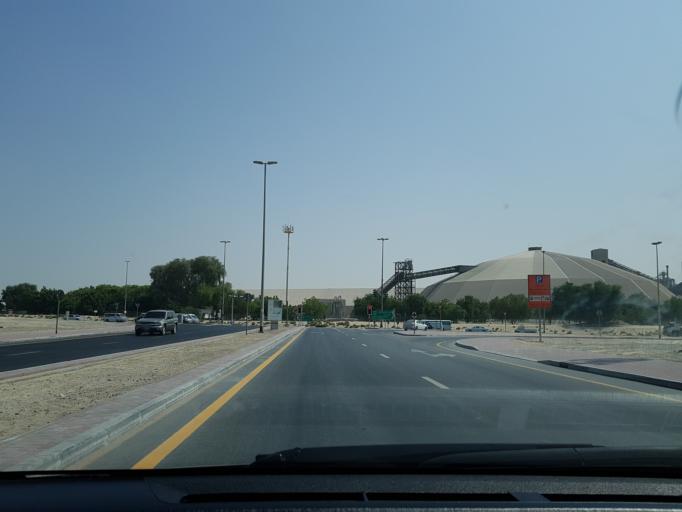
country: AE
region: Dubai
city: Dubai
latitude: 25.1611
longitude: 55.2396
